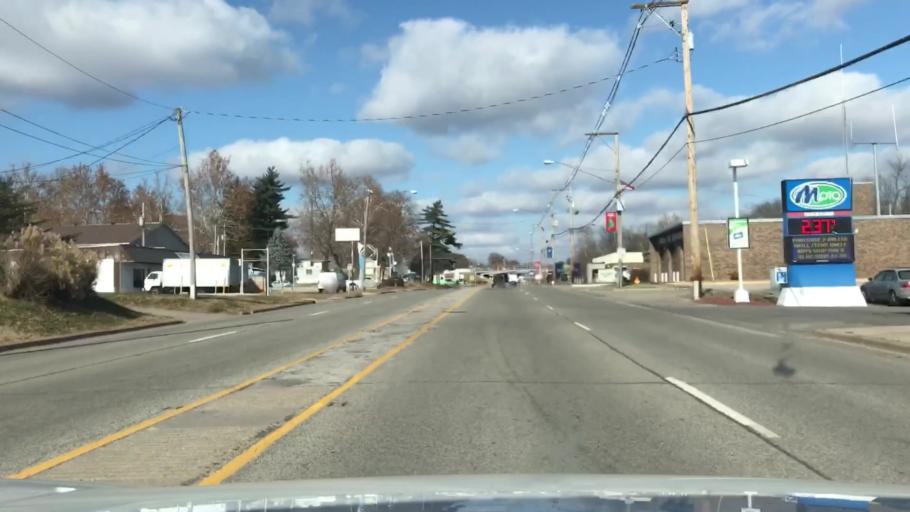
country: US
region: Illinois
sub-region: Saint Clair County
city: Belleville
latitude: 38.5262
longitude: -89.9842
